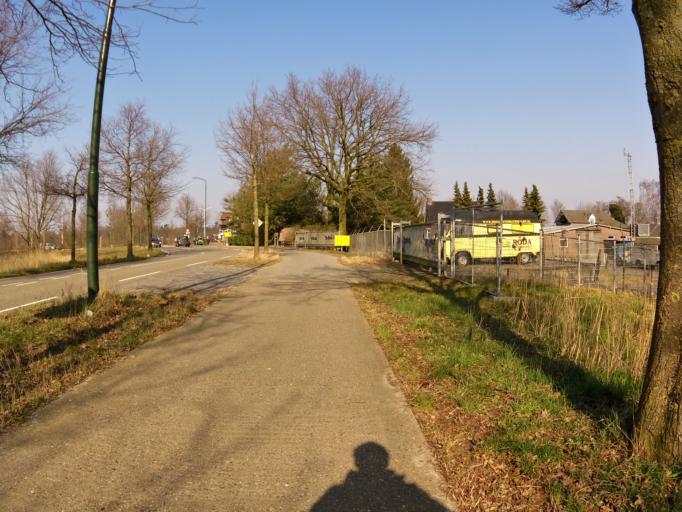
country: NL
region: North Brabant
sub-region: Gemeente Sint-Michielsgestel
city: Sint-Michielsgestel
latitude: 51.6890
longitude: 5.3750
